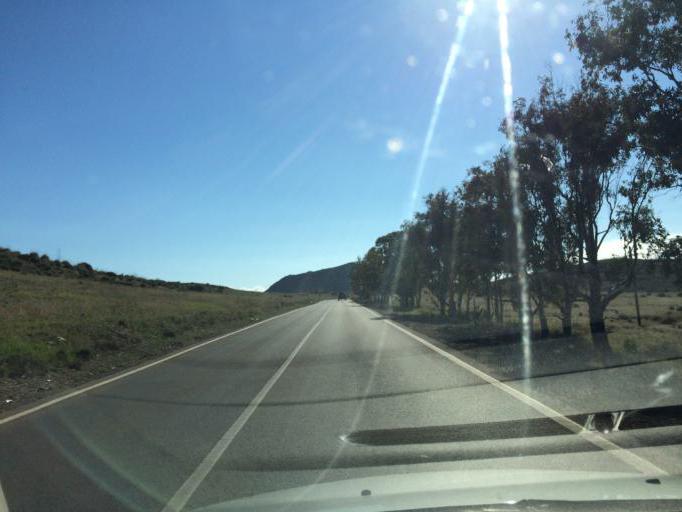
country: ES
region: Andalusia
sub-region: Provincia de Almeria
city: San Jose
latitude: 36.7851
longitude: -2.1084
